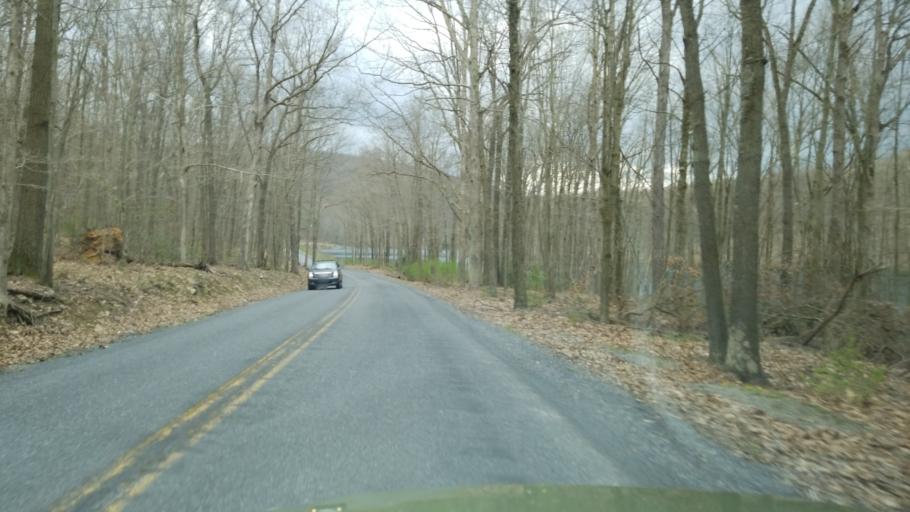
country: US
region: Pennsylvania
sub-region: Blair County
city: Tipton
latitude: 40.6817
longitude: -78.3288
